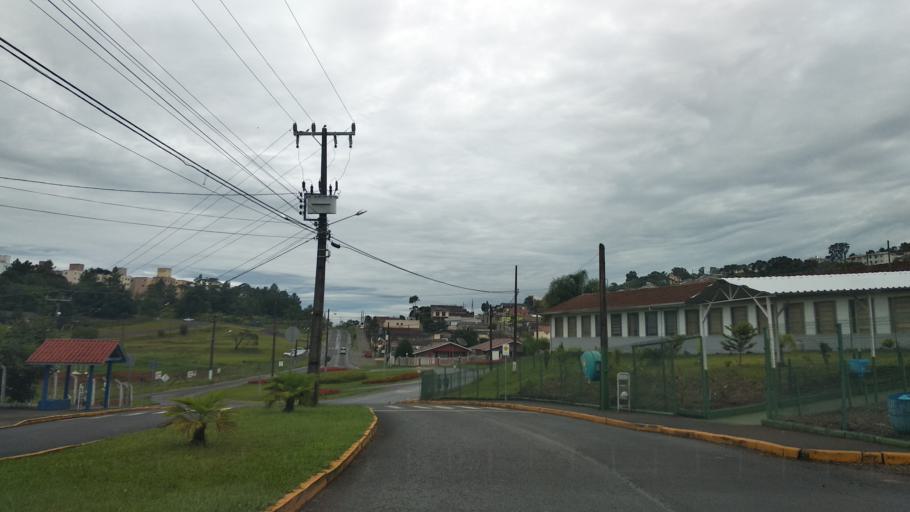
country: BR
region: Santa Catarina
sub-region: Videira
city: Videira
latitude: -26.9906
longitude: -51.1815
